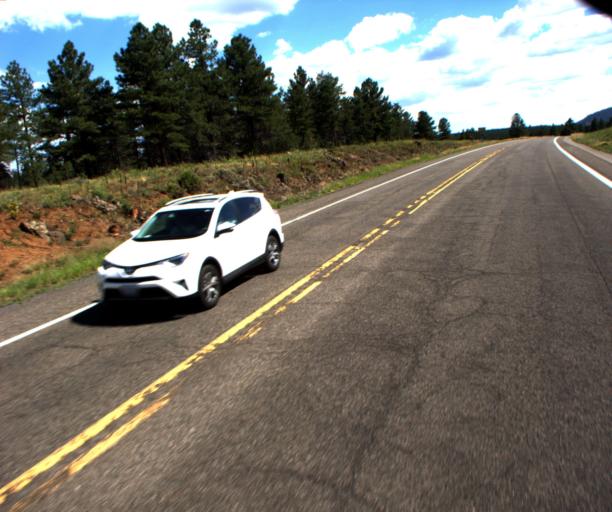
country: US
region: Arizona
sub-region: Coconino County
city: Williams
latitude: 35.2967
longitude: -112.1415
